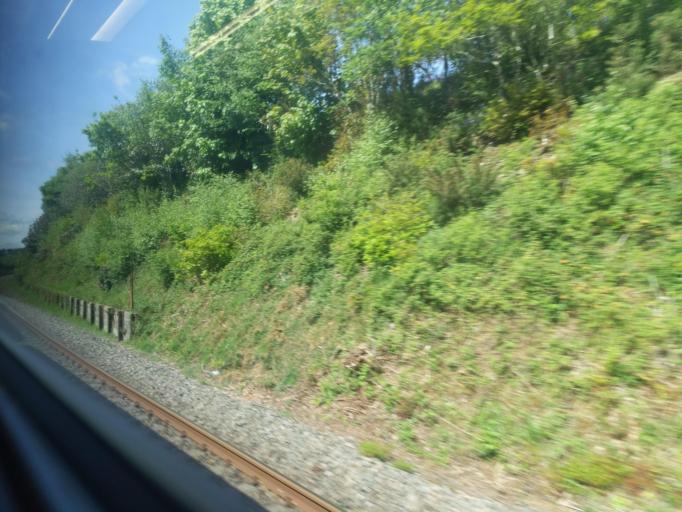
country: GB
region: England
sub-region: Cornwall
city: Liskeard
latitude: 50.4527
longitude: -4.5176
